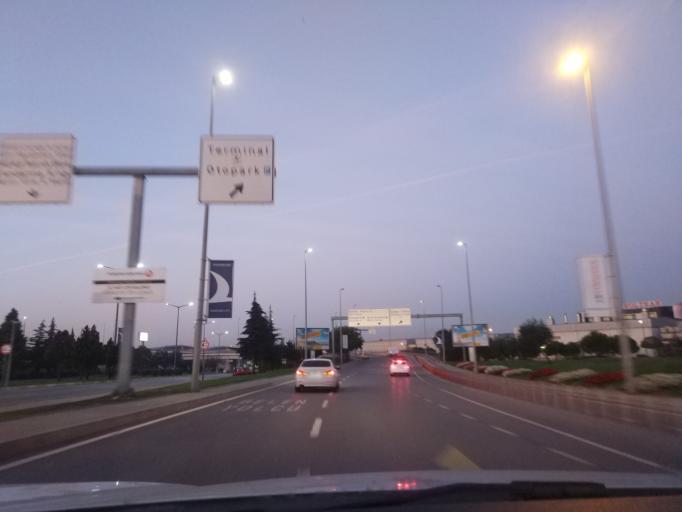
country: TR
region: Istanbul
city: Pendik
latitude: 40.9095
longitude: 29.3125
